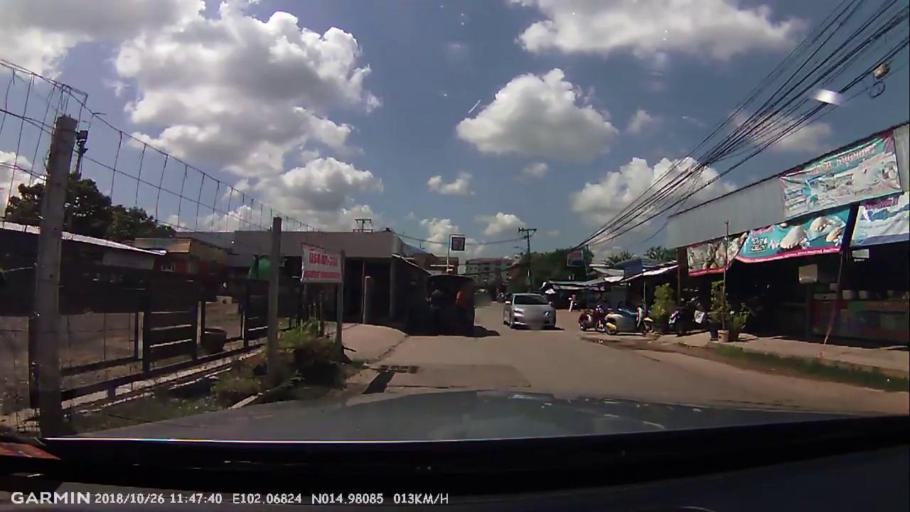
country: TH
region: Nakhon Ratchasima
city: Nakhon Ratchasima
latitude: 14.9808
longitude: 102.0682
